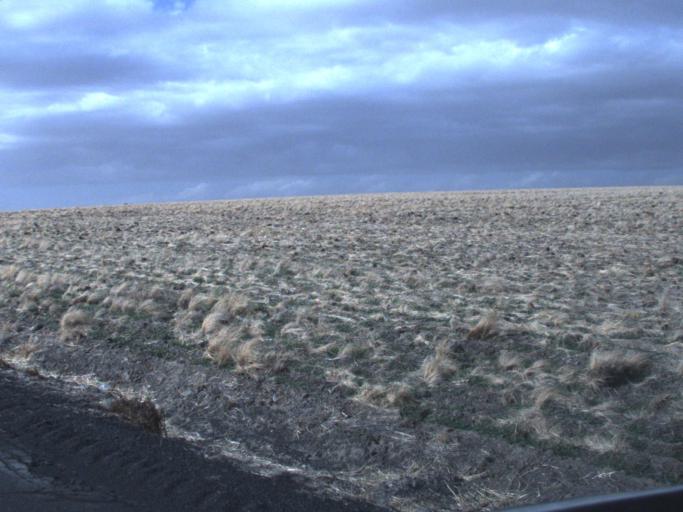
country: US
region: Washington
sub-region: Okanogan County
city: Coulee Dam
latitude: 47.6123
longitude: -118.7729
